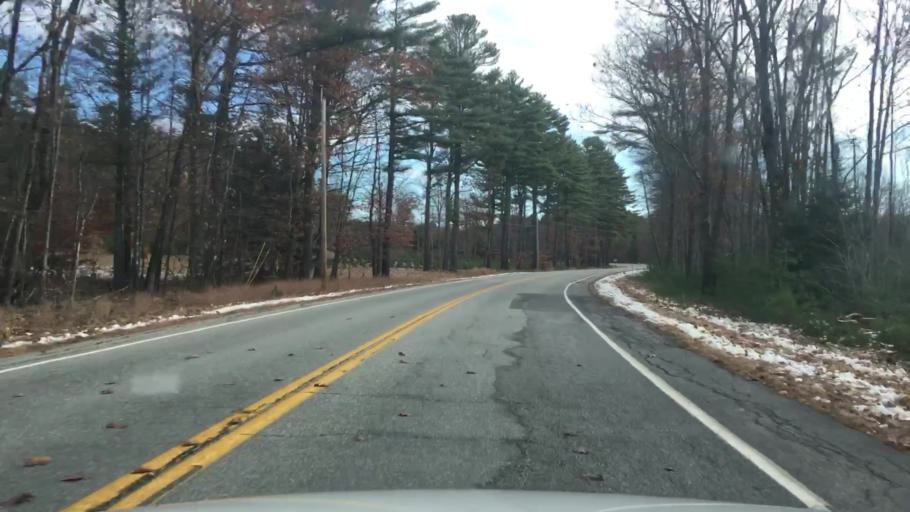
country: US
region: Maine
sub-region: Kennebec County
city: Wayne
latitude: 44.3514
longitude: -70.1059
